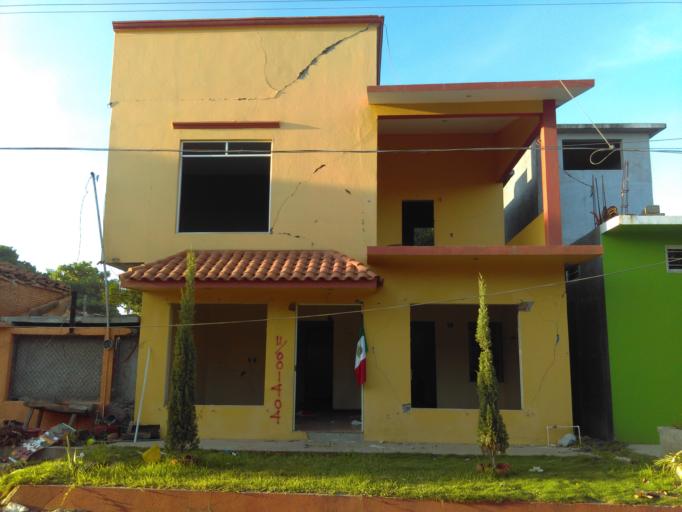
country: MX
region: Oaxaca
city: San Jeronimo Ixtepec
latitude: 16.5680
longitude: -95.1021
